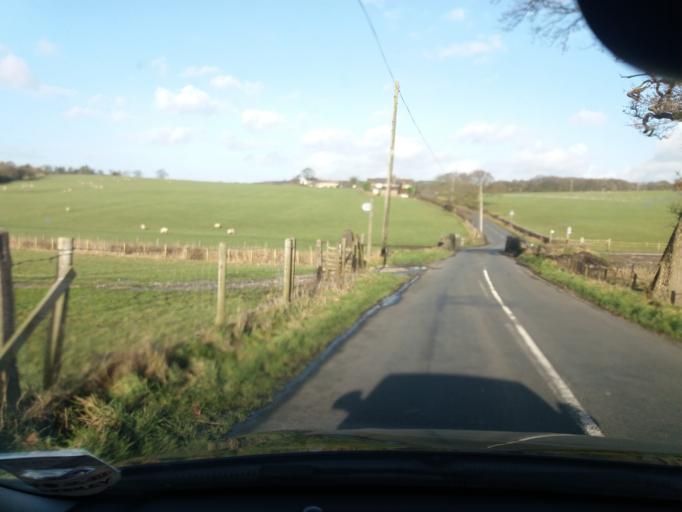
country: GB
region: England
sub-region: Lancashire
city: Adlington
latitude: 53.6303
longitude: -2.5835
